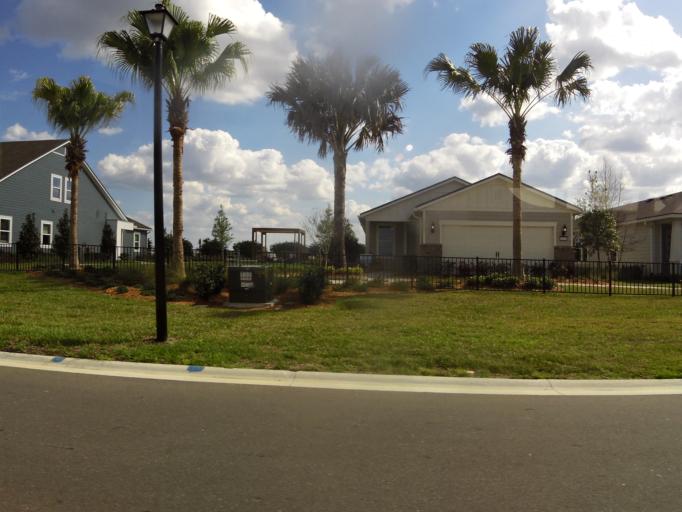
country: US
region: Florida
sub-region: Saint Johns County
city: Palm Valley
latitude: 30.1740
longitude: -81.5087
